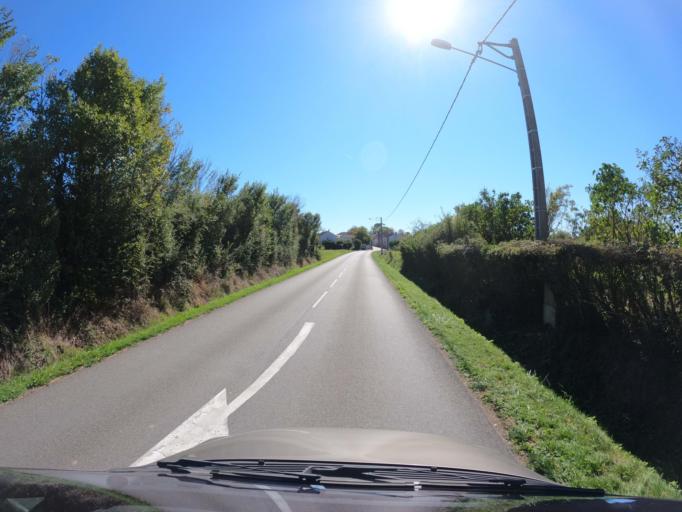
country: FR
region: Limousin
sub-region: Departement de la Haute-Vienne
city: Le Dorat
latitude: 46.2214
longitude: 1.0740
